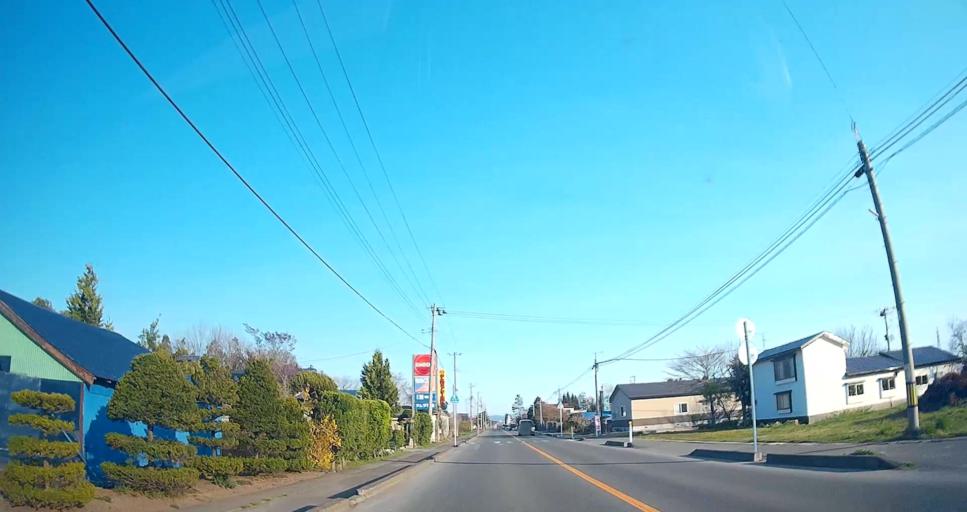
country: JP
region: Aomori
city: Mutsu
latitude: 41.2669
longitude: 141.2213
